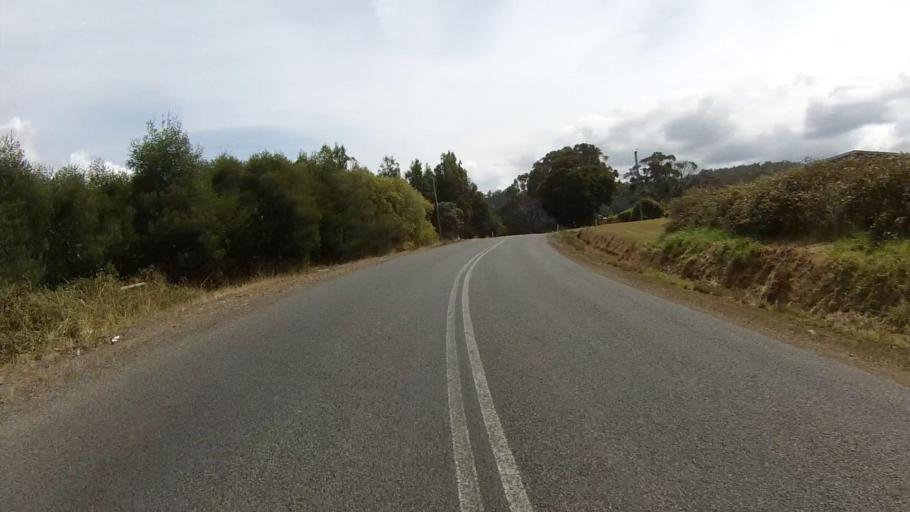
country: AU
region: Tasmania
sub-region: Huon Valley
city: Cygnet
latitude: -43.1896
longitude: 147.1005
